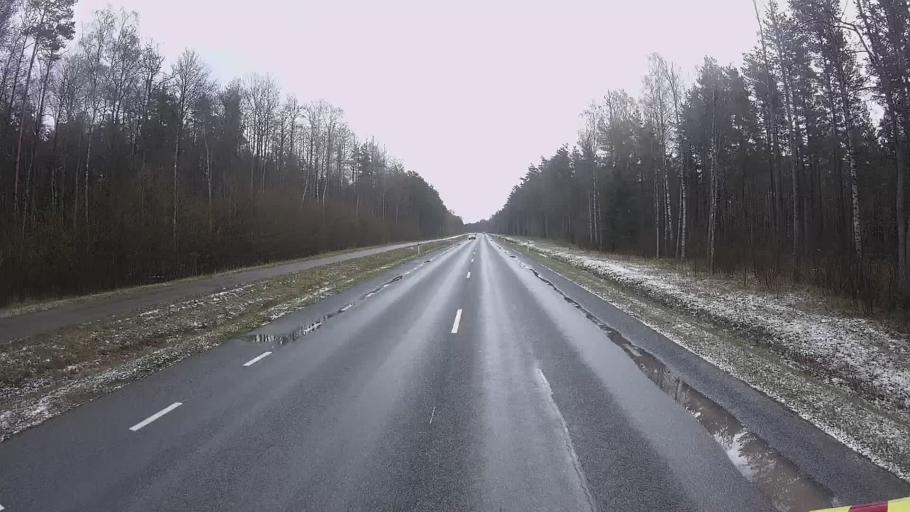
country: EE
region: Hiiumaa
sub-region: Kaerdla linn
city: Kardla
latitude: 59.0023
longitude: 22.6948
